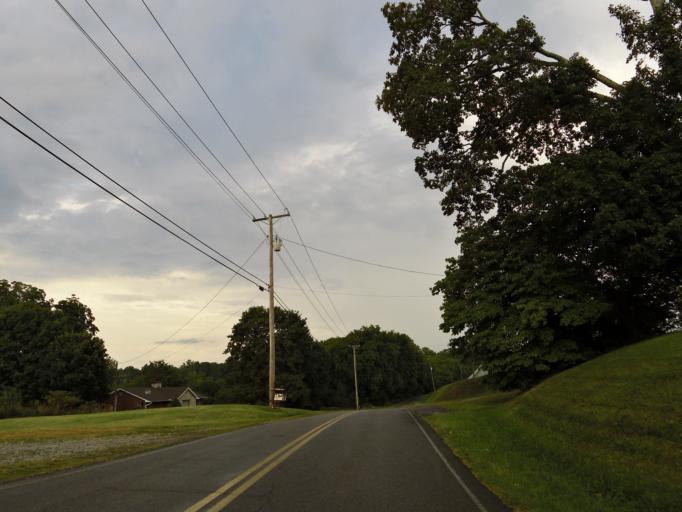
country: US
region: Tennessee
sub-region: Blount County
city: Wildwood
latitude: 35.8407
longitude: -83.8379
